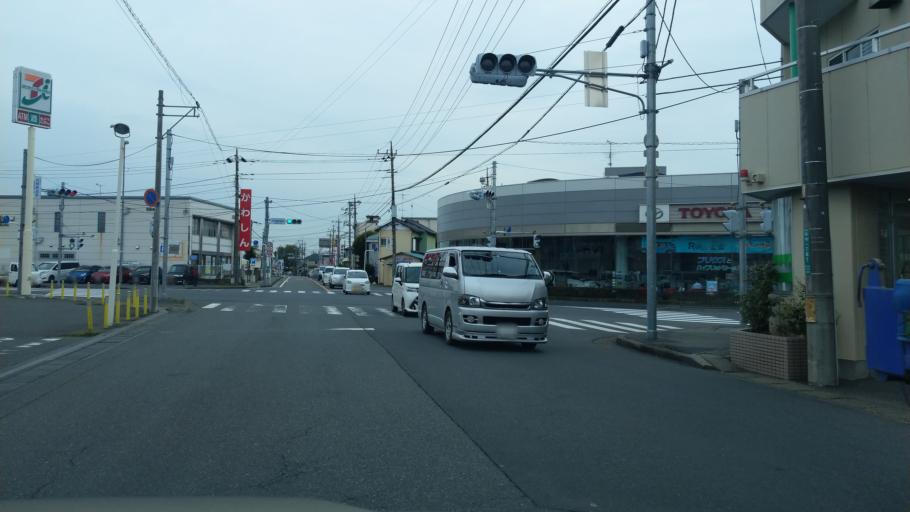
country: JP
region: Saitama
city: Iwatsuki
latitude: 35.9433
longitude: 139.7079
